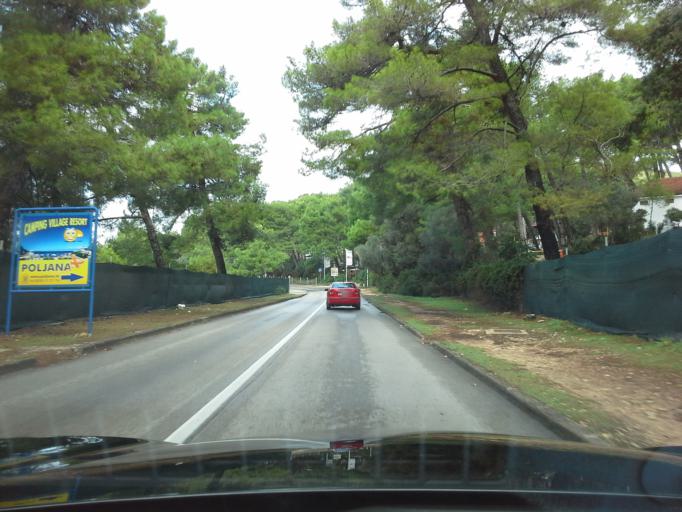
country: HR
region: Primorsko-Goranska
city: Mali Losinj
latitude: 44.5545
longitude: 14.4424
